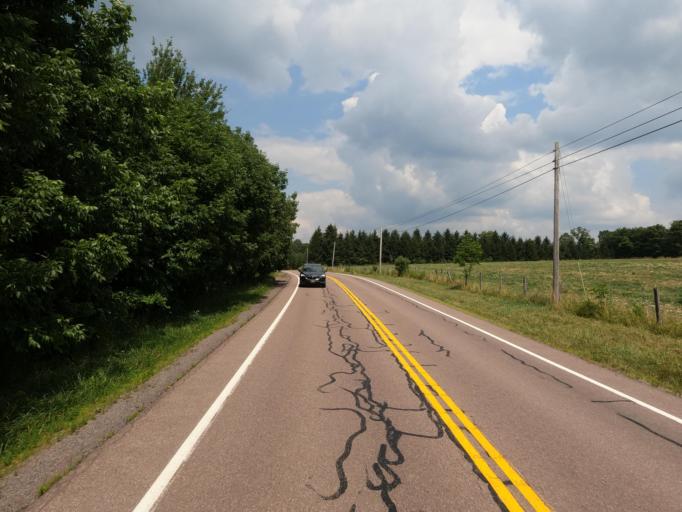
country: US
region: Maryland
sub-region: Allegany County
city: Westernport
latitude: 39.6390
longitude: -79.2038
